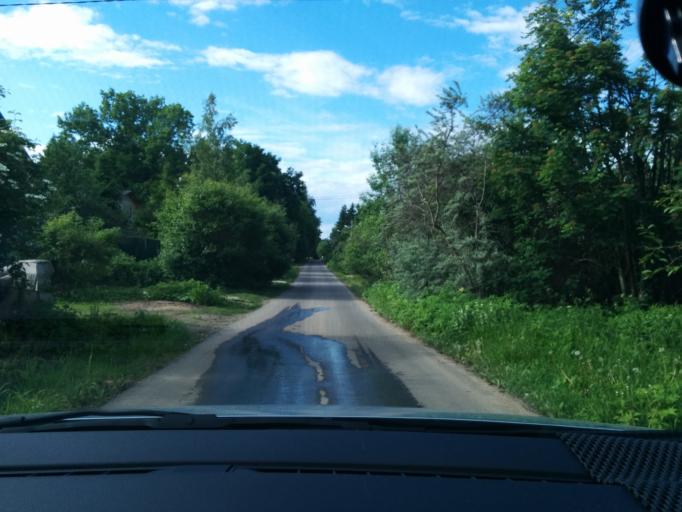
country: RU
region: Moskovskaya
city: Lugovaya
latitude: 56.0549
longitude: 37.4783
